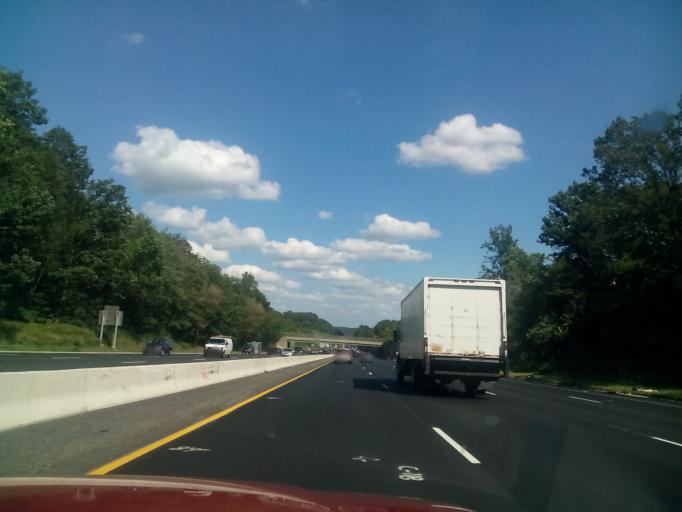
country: US
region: New Jersey
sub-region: Morris County
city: Rockaway
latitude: 40.9109
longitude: -74.5308
